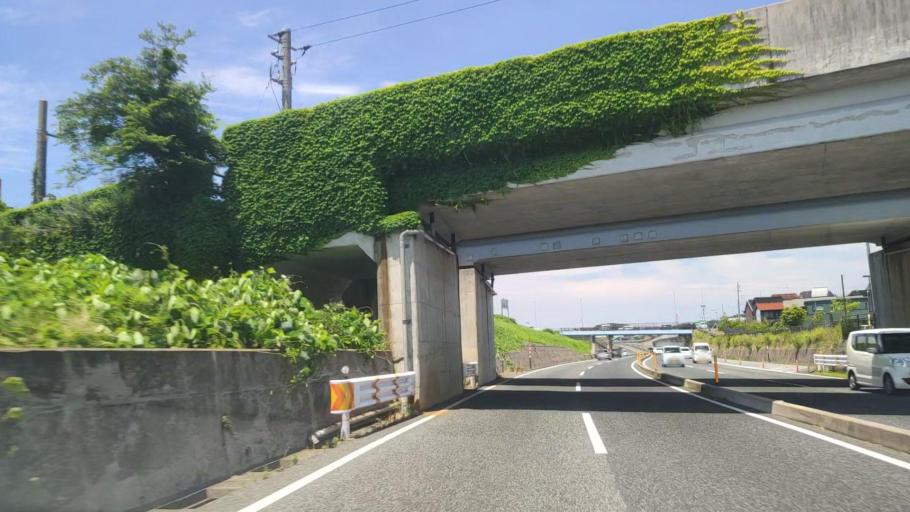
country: JP
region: Tottori
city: Tottori
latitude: 35.4976
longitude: 134.2174
